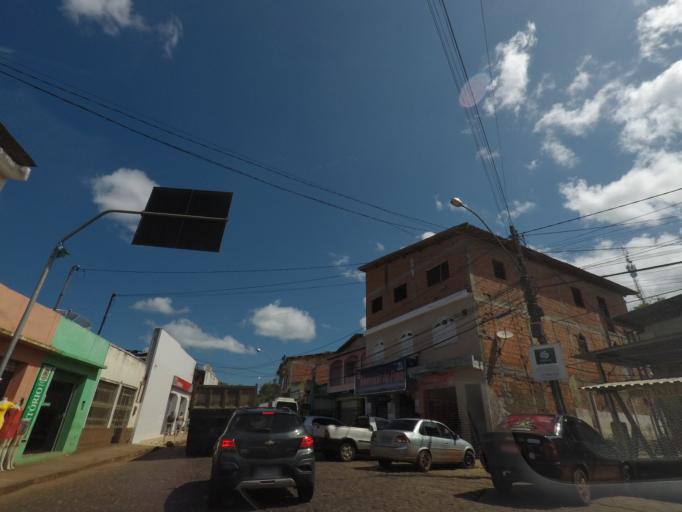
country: BR
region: Bahia
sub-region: Taperoa
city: Taperoa
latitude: -13.6004
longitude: -39.1062
